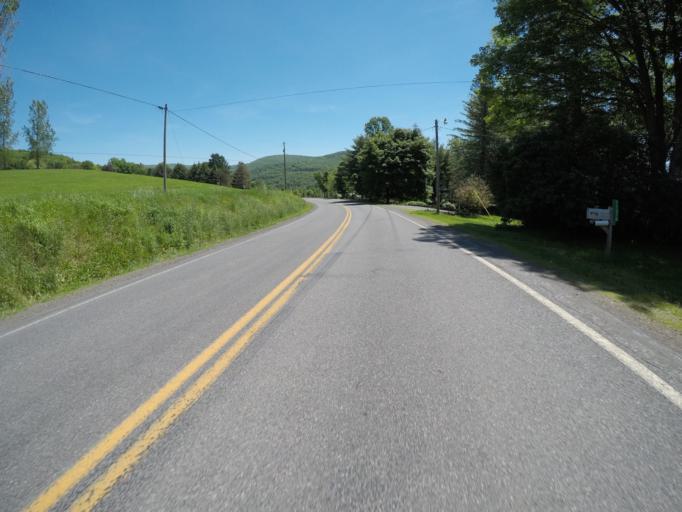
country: US
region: New York
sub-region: Delaware County
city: Delhi
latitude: 42.1828
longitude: -74.7985
